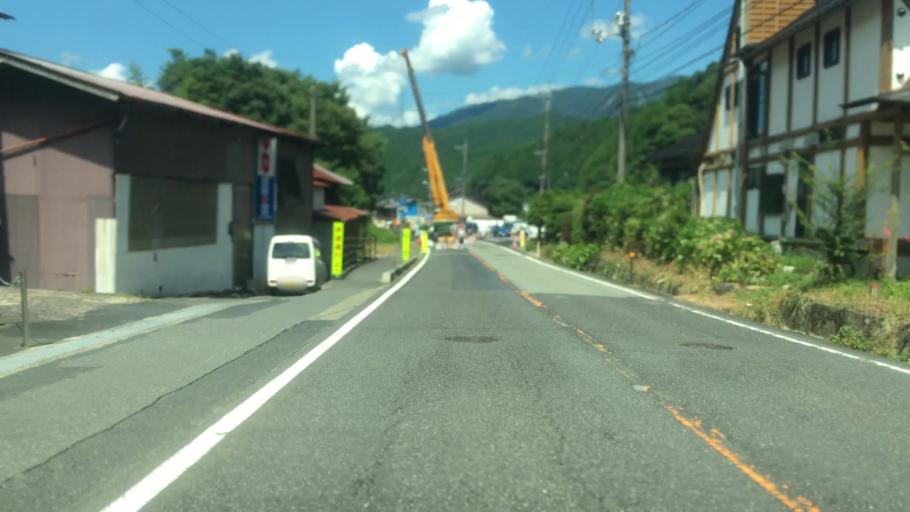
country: JP
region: Okayama
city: Tsuyama
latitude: 35.2163
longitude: 134.2188
